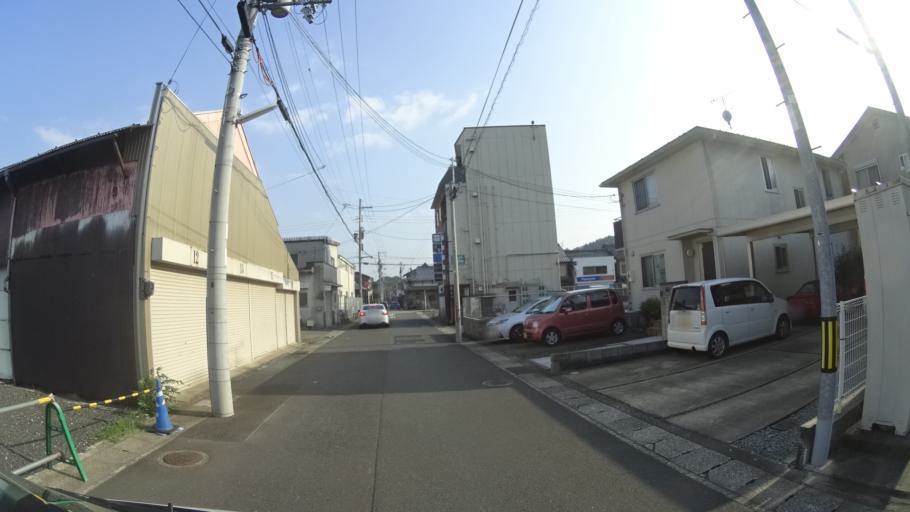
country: JP
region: Kyoto
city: Maizuru
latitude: 35.4437
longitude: 135.3261
